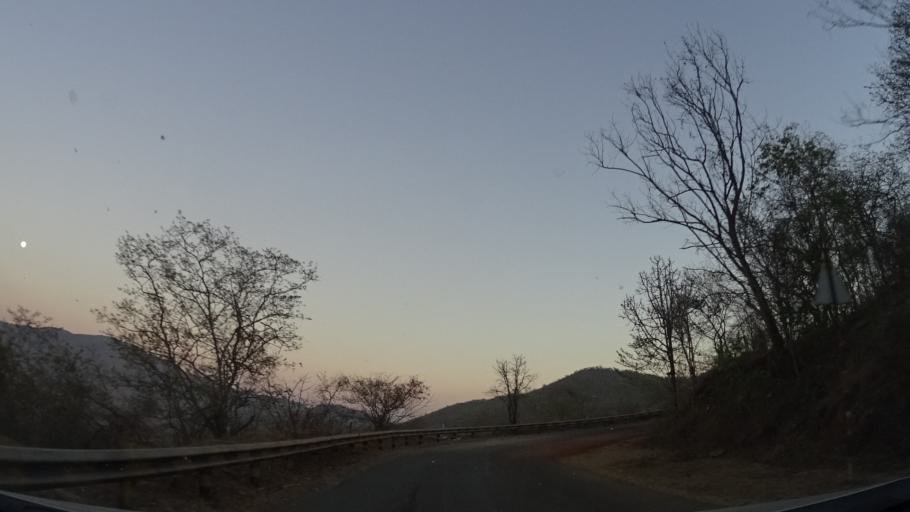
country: IN
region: Karnataka
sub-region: Chikmagalur
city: Birur
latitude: 13.5397
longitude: 75.8211
